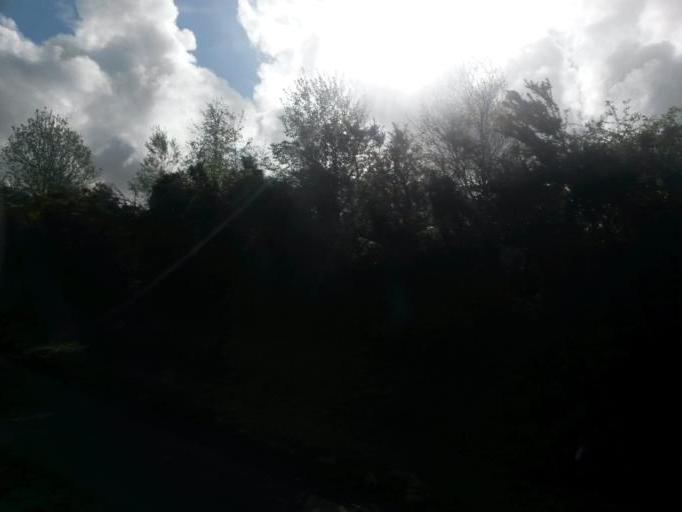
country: IE
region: Leinster
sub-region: Loch Garman
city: Gorey
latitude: 52.6427
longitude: -6.3365
